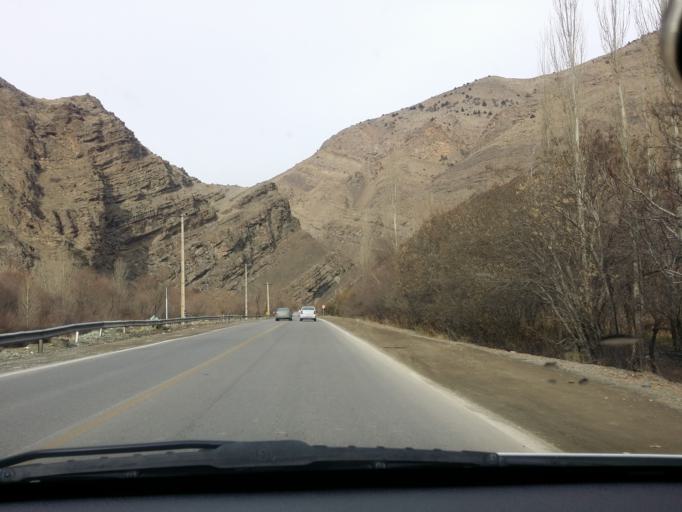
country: IR
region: Tehran
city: Tajrish
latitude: 36.0155
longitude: 51.2810
